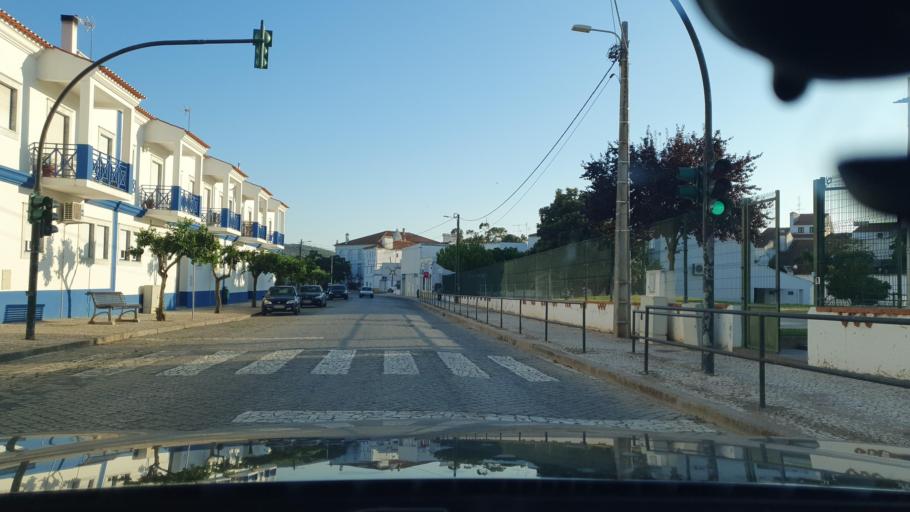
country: PT
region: Portalegre
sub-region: Fronteira
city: Fronteira
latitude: 38.9519
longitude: -7.6749
